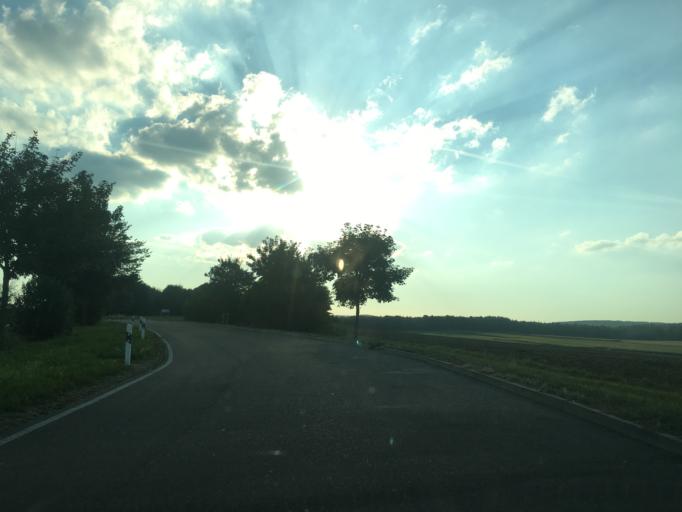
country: DE
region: Baden-Wuerttemberg
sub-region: Tuebingen Region
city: Munderkingen
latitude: 48.2545
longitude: 9.6384
